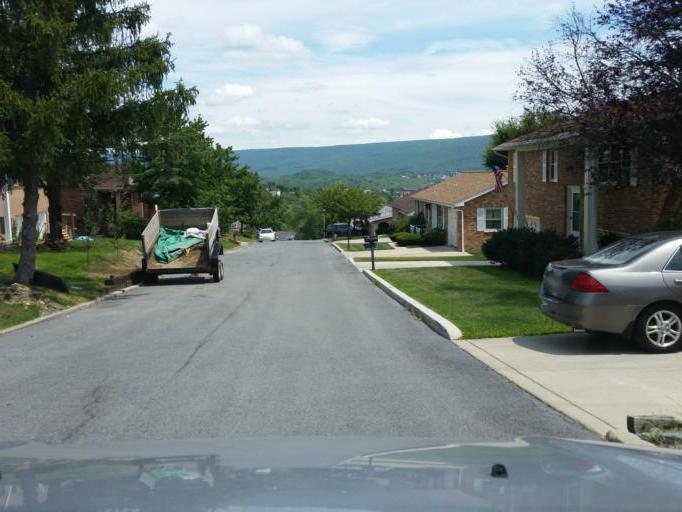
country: US
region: Pennsylvania
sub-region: Blair County
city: Altoona
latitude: 40.5358
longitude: -78.4087
